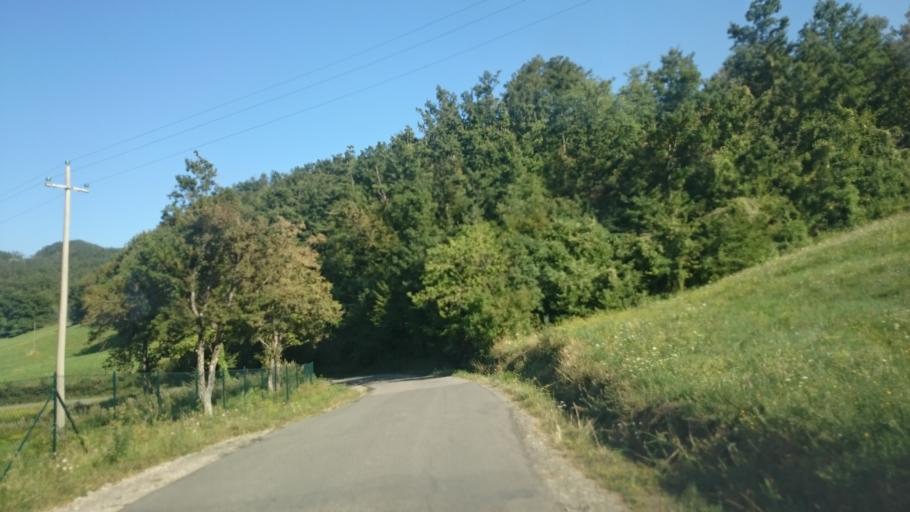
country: IT
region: Emilia-Romagna
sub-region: Provincia di Reggio Emilia
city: Villa Minozzo
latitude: 44.3369
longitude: 10.4746
